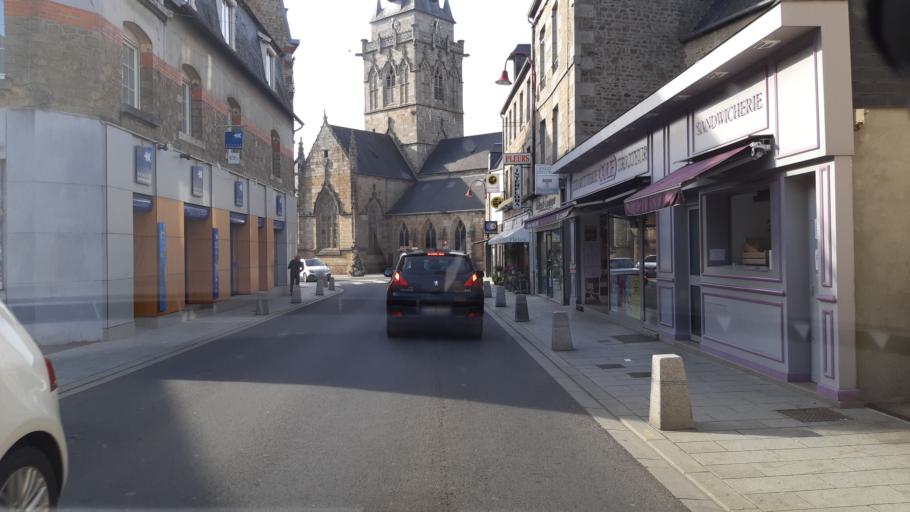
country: FR
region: Lower Normandy
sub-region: Departement de la Manche
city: Villedieu-les-Poeles
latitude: 48.8373
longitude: -1.2220
